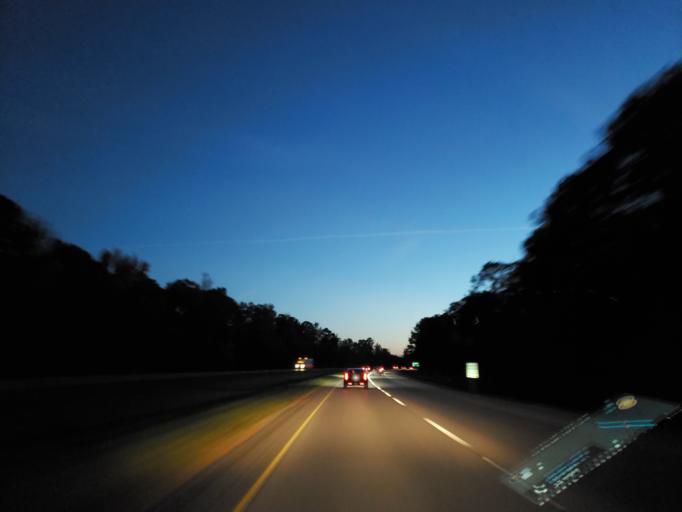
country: US
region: Mississippi
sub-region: Clarke County
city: Stonewall
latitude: 32.2227
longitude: -88.8333
